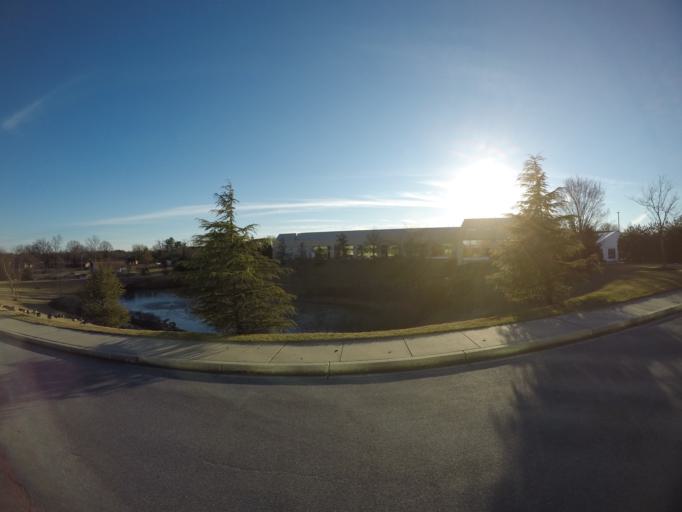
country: US
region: Maryland
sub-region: Howard County
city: Ilchester
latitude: 39.2097
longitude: -76.7965
